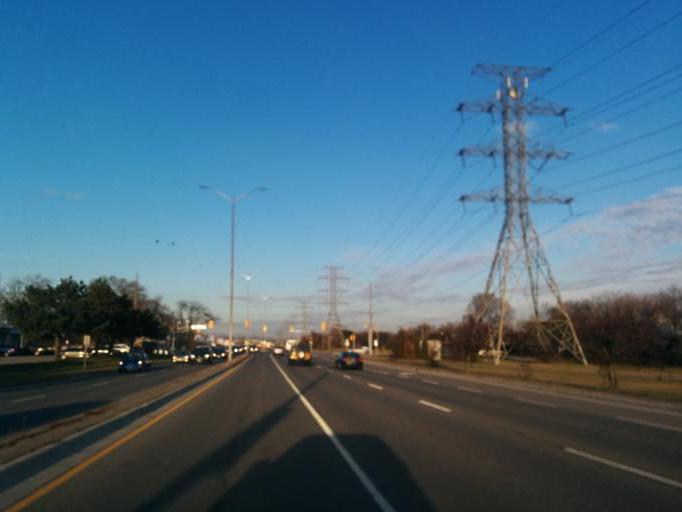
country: CA
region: Ontario
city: Etobicoke
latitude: 43.5965
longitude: -79.5829
